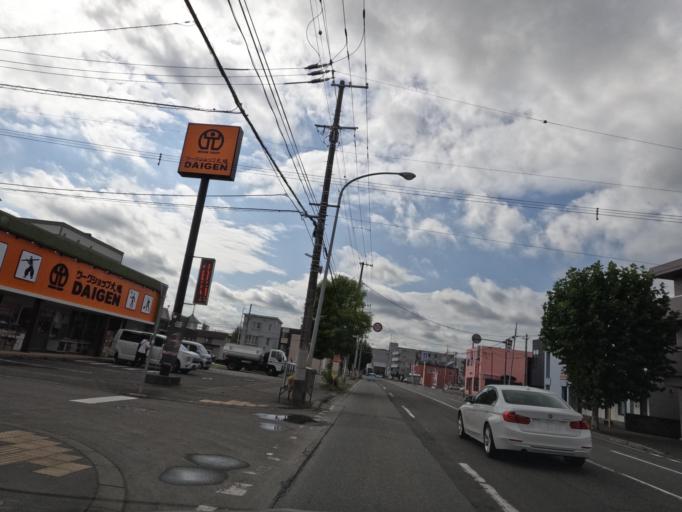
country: JP
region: Hokkaido
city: Chitose
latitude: 42.8192
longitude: 141.6530
